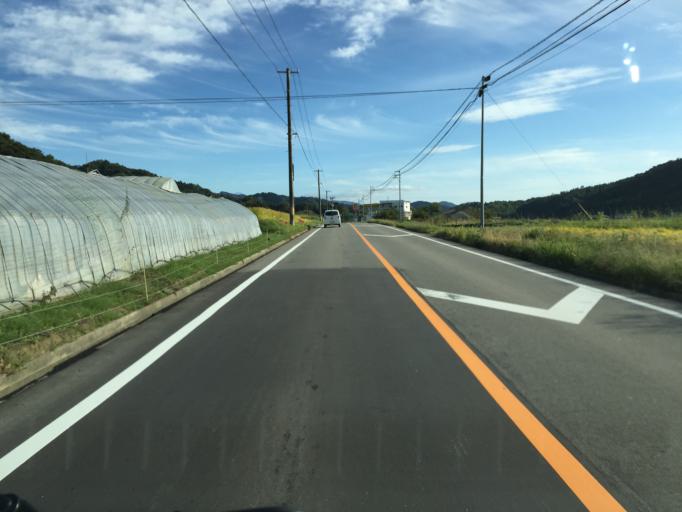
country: JP
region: Fukushima
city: Yanagawamachi-saiwaicho
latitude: 37.8105
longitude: 140.6188
